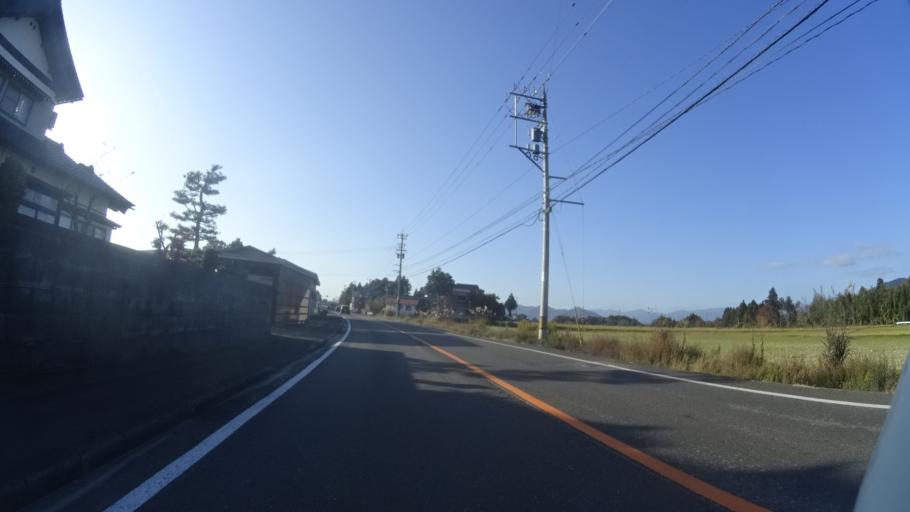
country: JP
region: Fukui
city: Ono
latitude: 35.9729
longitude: 136.5596
